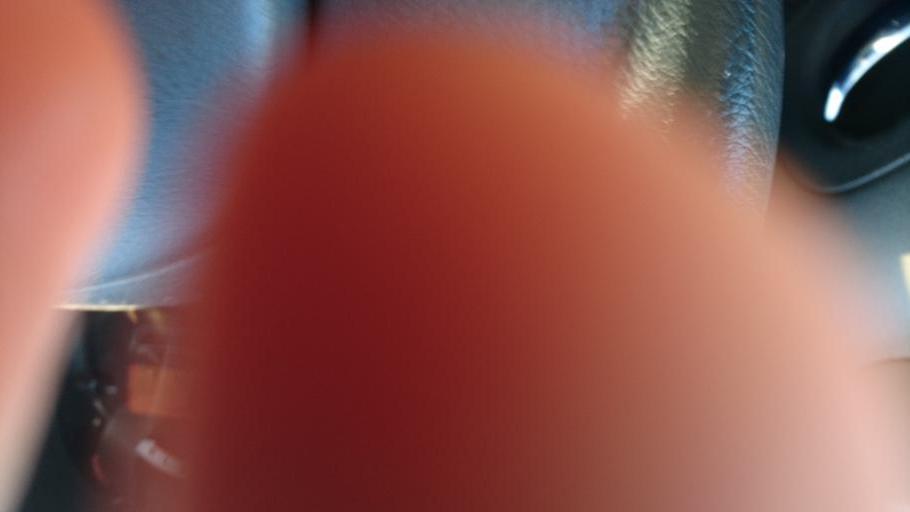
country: SE
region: Skane
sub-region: Tomelilla Kommun
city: Tomelilla
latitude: 55.5039
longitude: 14.0306
